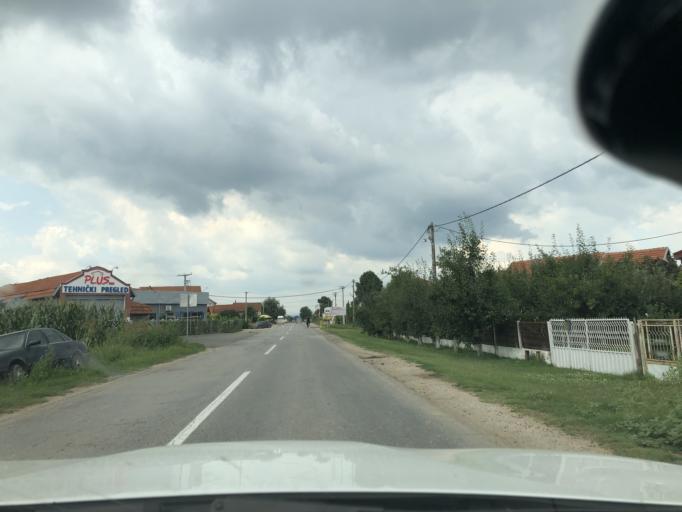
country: RS
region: Central Serbia
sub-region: Jablanicki Okrug
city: Leskovac
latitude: 42.9706
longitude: 21.8812
